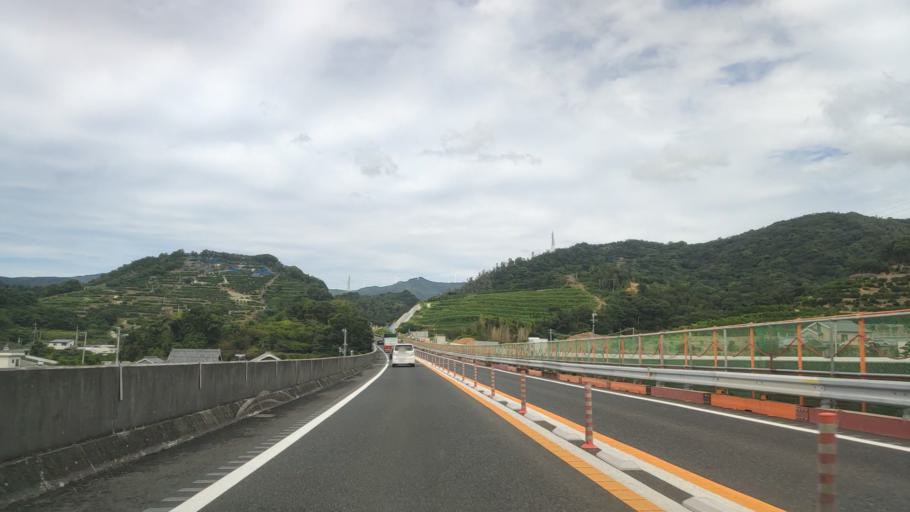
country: JP
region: Wakayama
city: Gobo
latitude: 33.9142
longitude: 135.1943
